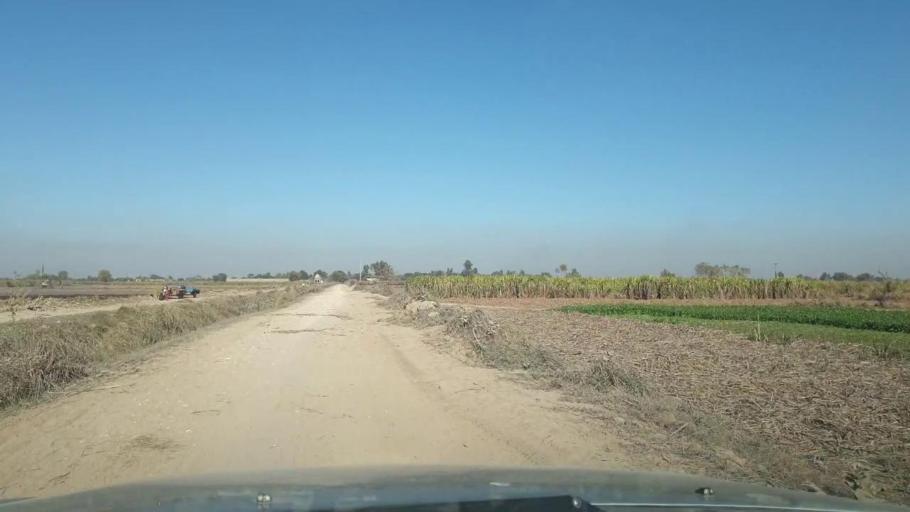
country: PK
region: Sindh
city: Ghotki
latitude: 28.0374
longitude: 69.2465
